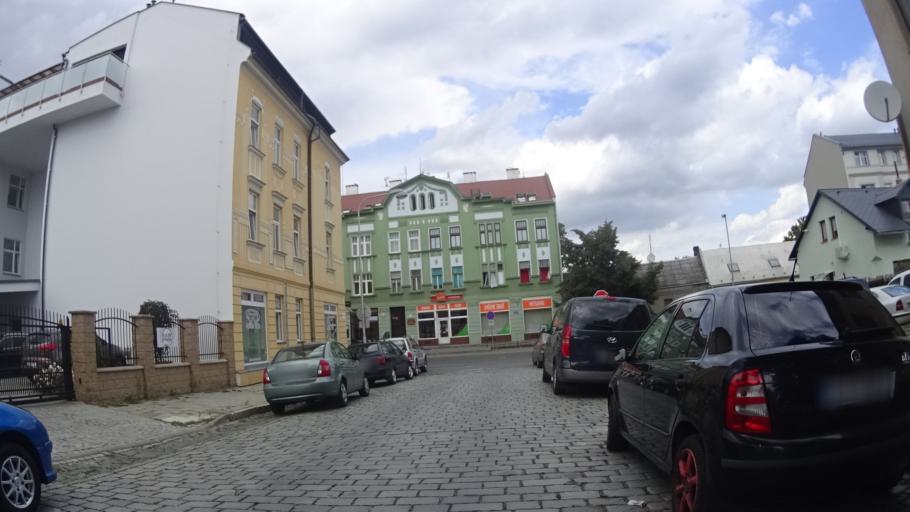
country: CZ
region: Olomoucky
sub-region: Okres Olomouc
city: Olomouc
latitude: 49.6045
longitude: 17.2407
